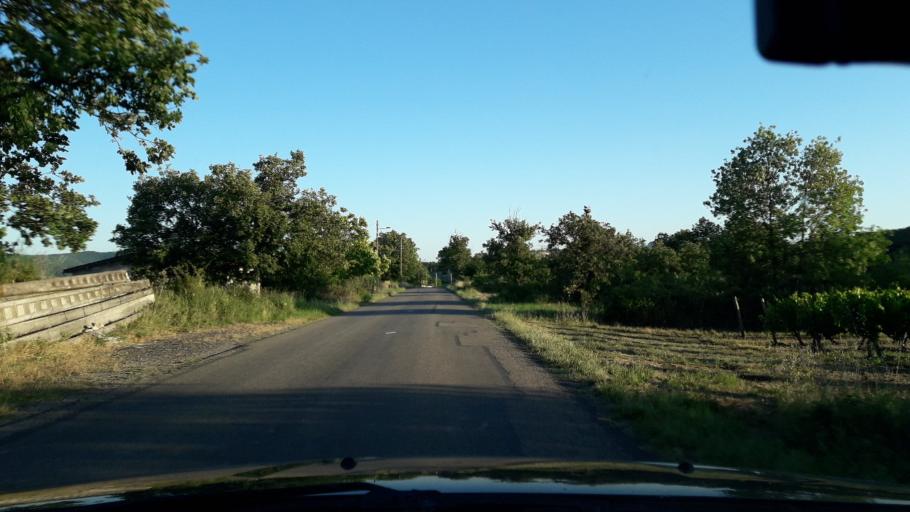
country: FR
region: Rhone-Alpes
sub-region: Departement de l'Ardeche
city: Lavilledieu
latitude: 44.5944
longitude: 4.4604
